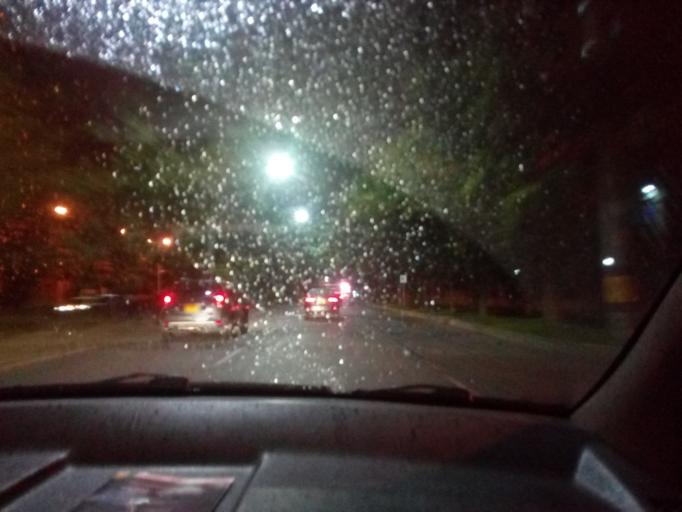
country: CO
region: Antioquia
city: Envigado
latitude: 6.1775
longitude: -75.5896
